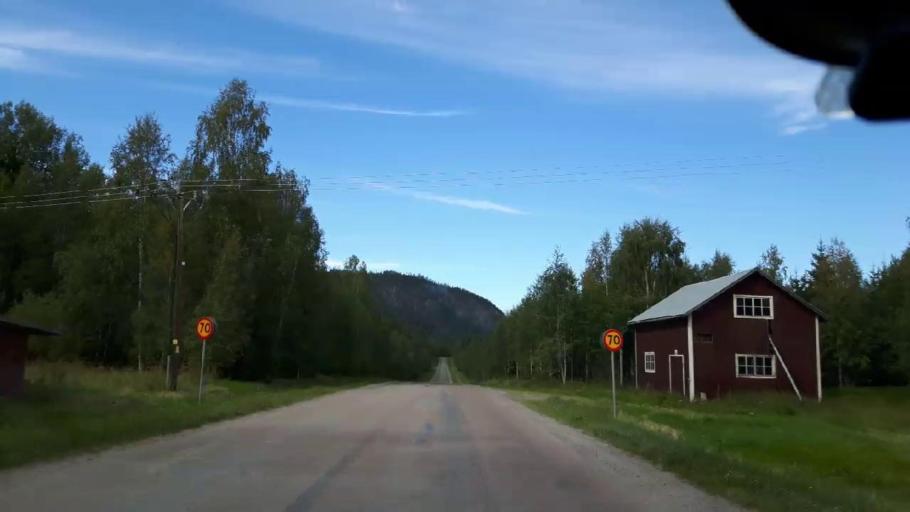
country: SE
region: Jaemtland
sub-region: Ragunda Kommun
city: Hammarstrand
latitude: 63.1180
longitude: 16.3386
